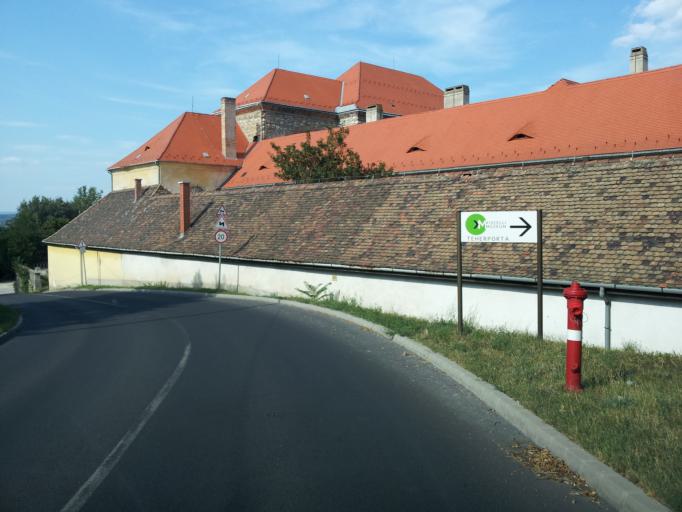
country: HU
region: Budapest
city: Budapest III. keruelet
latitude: 47.5378
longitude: 19.0274
